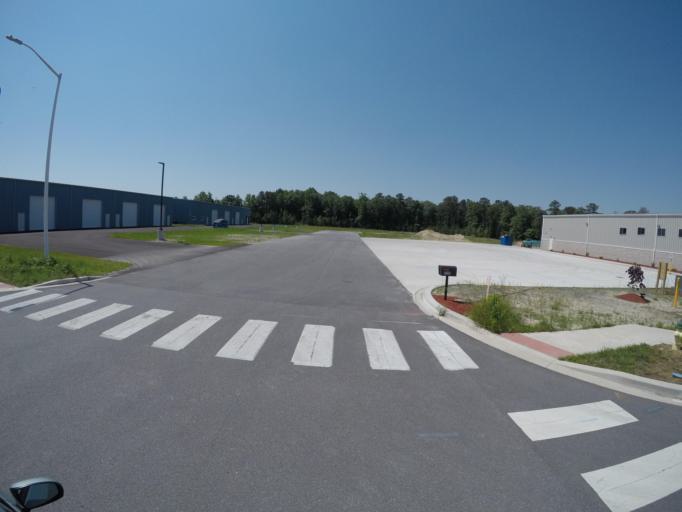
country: US
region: Delaware
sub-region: Sussex County
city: Georgetown
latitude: 38.6938
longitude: -75.3464
